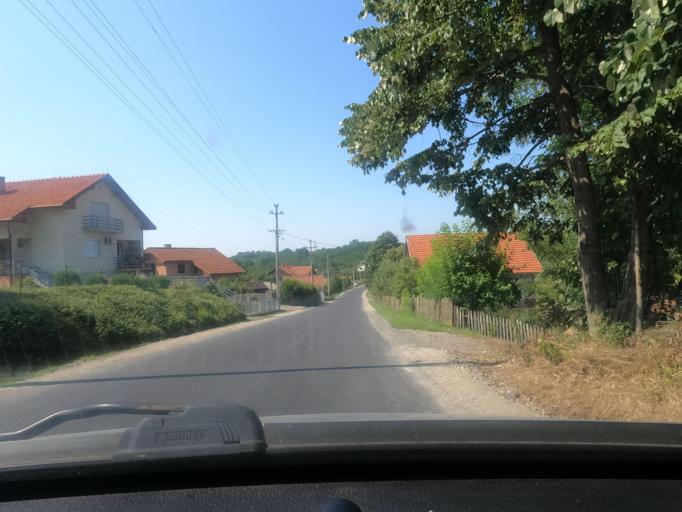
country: RS
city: Kozjak
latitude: 44.5690
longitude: 19.2867
